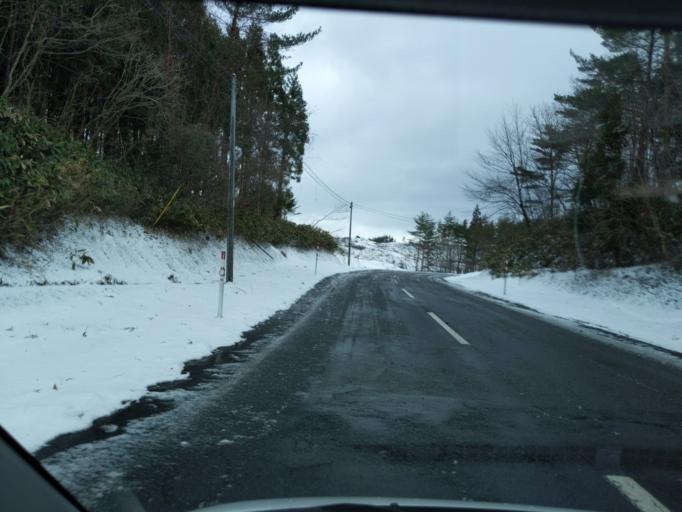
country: JP
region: Iwate
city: Ichinoseki
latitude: 38.9889
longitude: 140.9501
